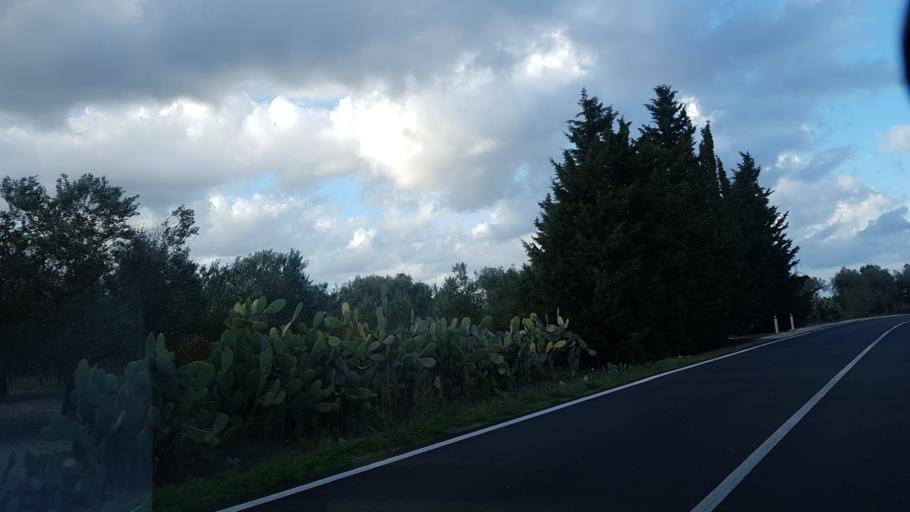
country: IT
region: Apulia
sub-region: Provincia di Brindisi
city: San Pietro Vernotico
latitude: 40.5145
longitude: 18.0113
